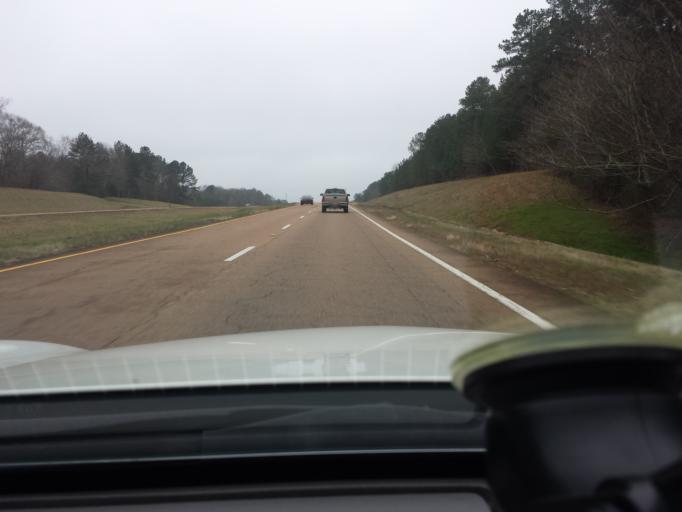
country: US
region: Mississippi
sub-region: Leake County
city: Carthage
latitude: 32.8423
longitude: -89.4645
